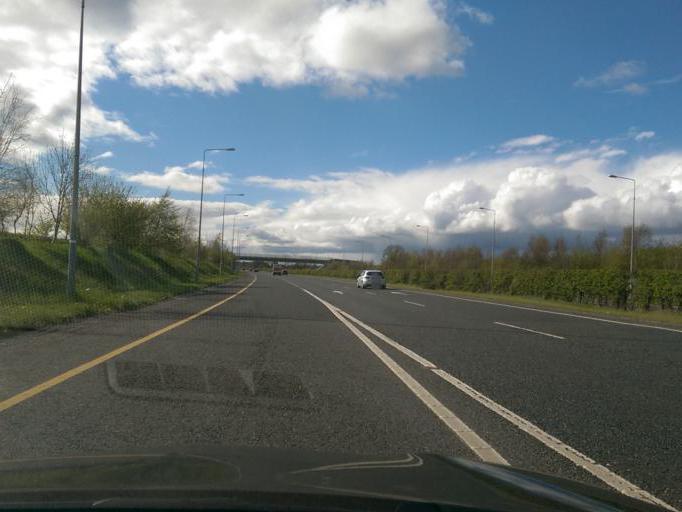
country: IE
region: Leinster
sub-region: Kildare
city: Kilcock
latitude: 53.4043
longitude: -6.6953
